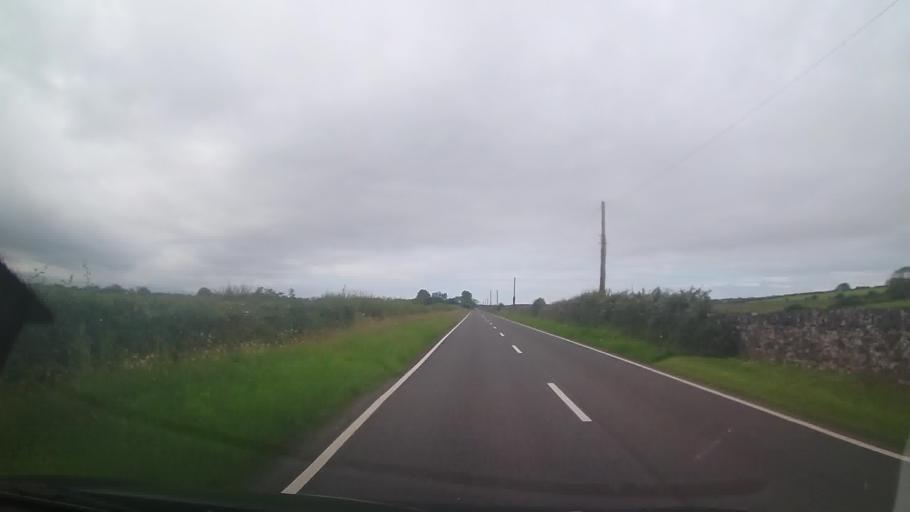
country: GB
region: Wales
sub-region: Gwynedd
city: Caernarfon
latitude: 53.1647
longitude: -4.3385
